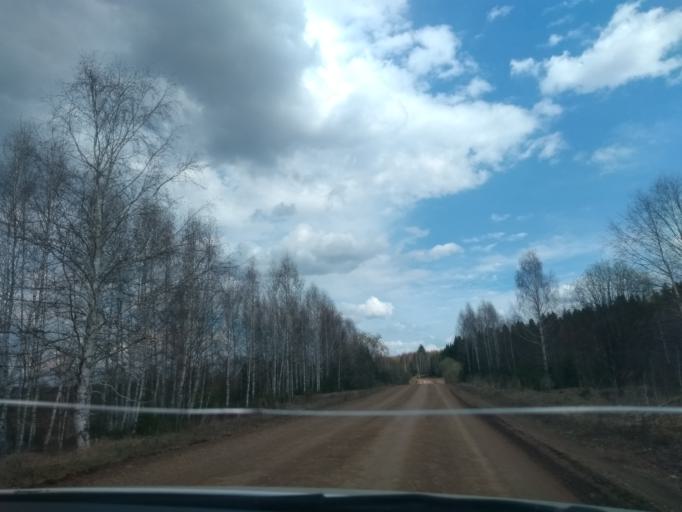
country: RU
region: Perm
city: Sylva
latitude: 57.8402
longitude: 56.7384
